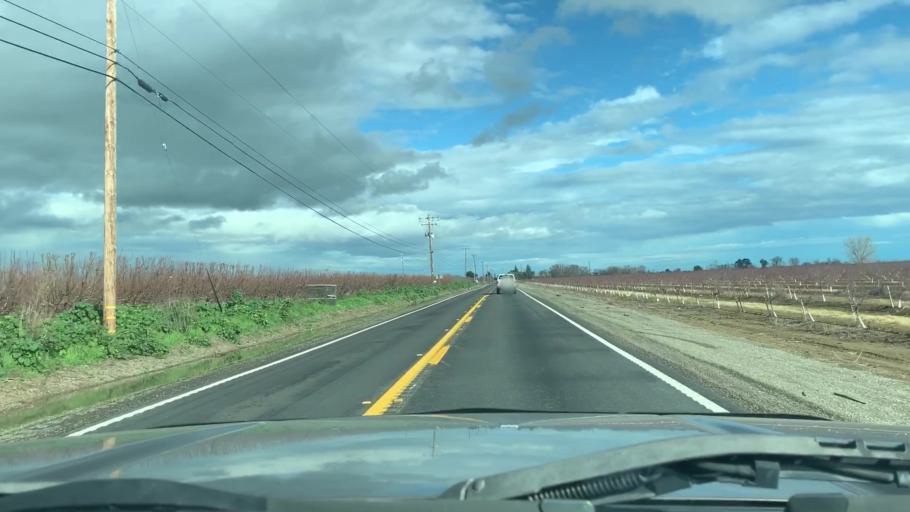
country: US
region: California
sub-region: Merced County
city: Gustine
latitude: 37.1233
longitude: -121.0153
